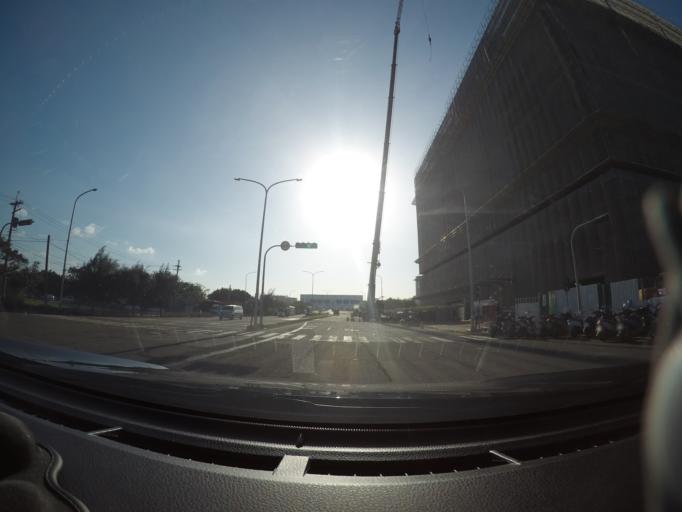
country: TW
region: Taiwan
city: Taoyuan City
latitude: 25.0929
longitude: 121.2557
